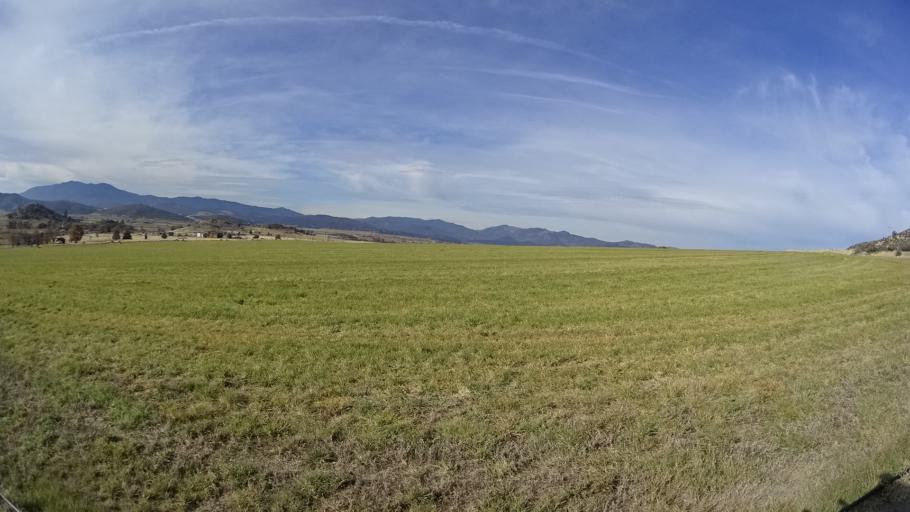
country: US
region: California
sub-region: Siskiyou County
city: Montague
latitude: 41.7068
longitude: -122.5155
